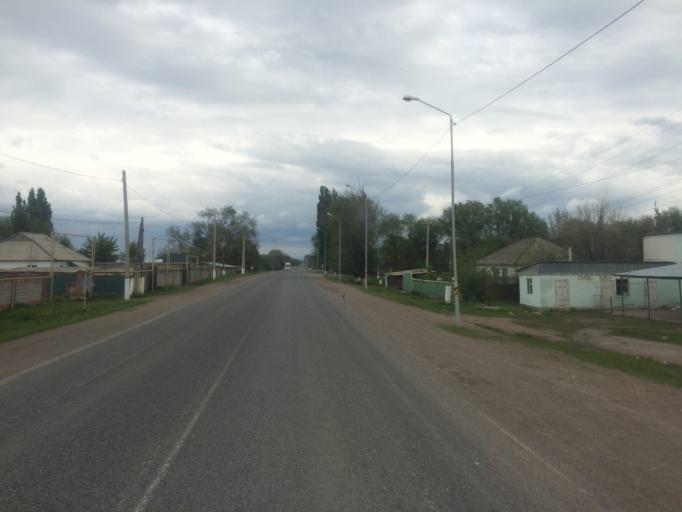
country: KZ
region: Zhambyl
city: Georgiyevka
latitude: 43.2272
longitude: 74.3960
